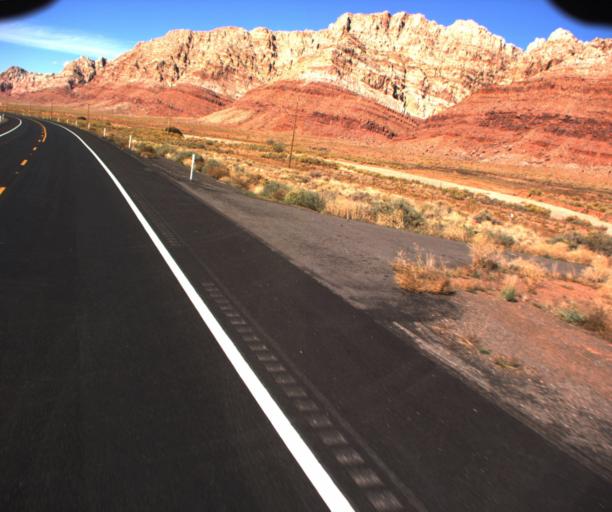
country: US
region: Arizona
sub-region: Coconino County
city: LeChee
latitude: 36.5059
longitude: -111.5837
